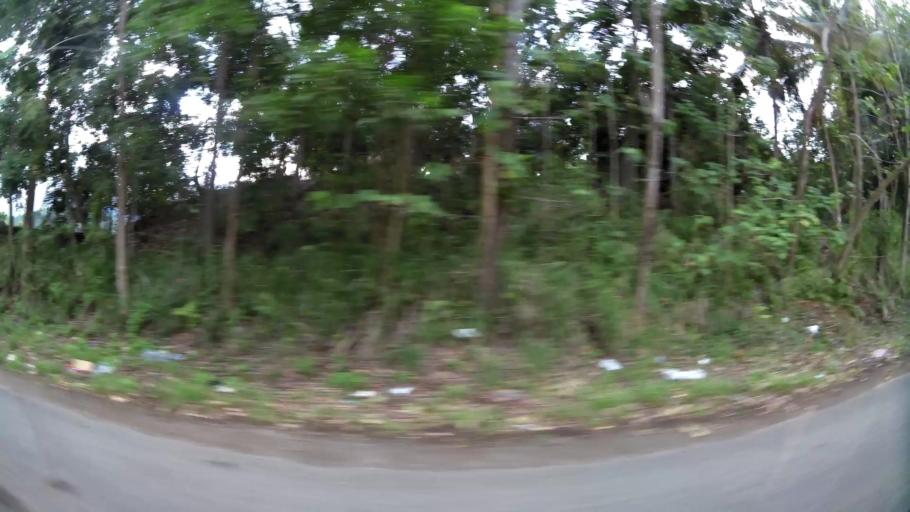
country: DO
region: San Cristobal
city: Villa Altagracia
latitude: 18.6492
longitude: -70.1694
